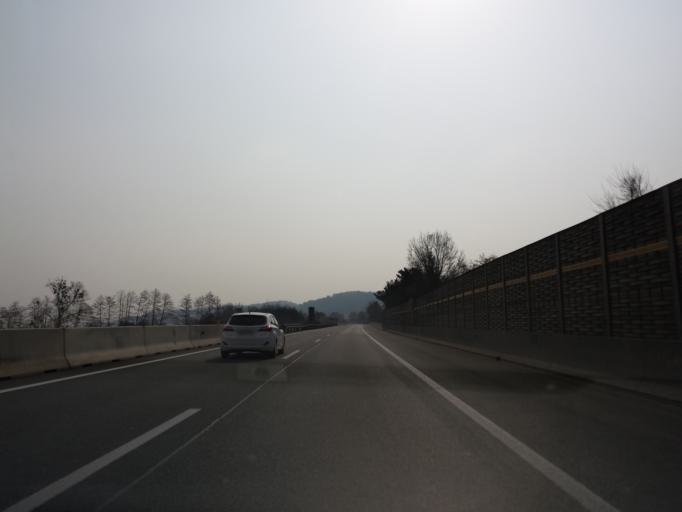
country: AT
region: Styria
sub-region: Politischer Bezirk Hartberg-Fuerstenfeld
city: Nestelbach im Ilztal
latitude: 47.0856
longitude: 15.8742
